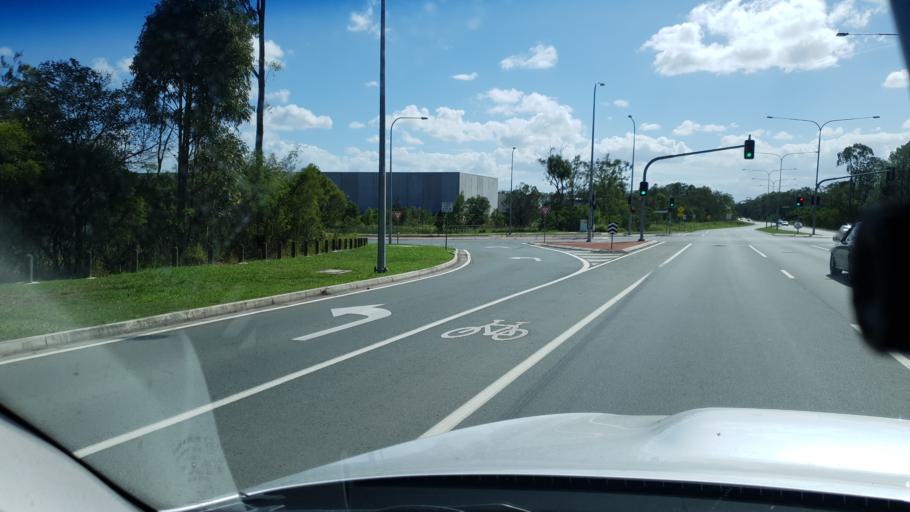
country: AU
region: Queensland
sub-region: Logan
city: Woodridge
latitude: -27.6453
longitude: 153.0950
